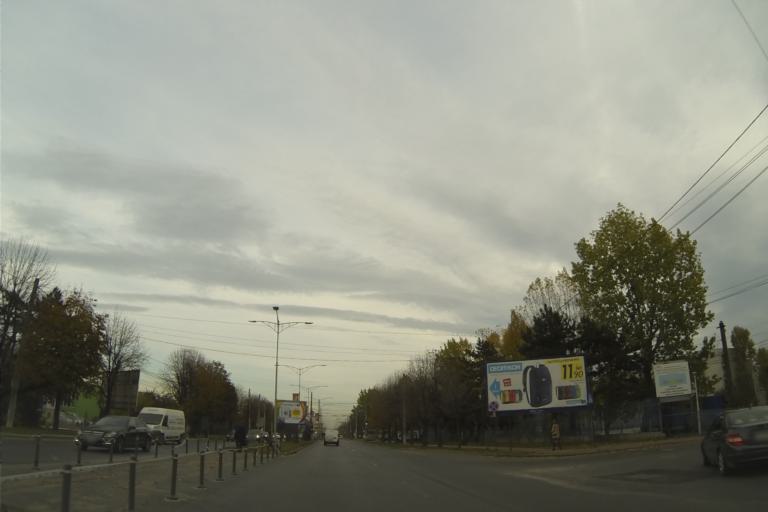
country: RO
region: Ilfov
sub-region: Comuna Chiajna
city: Chiajna
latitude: 44.4357
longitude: 25.9740
